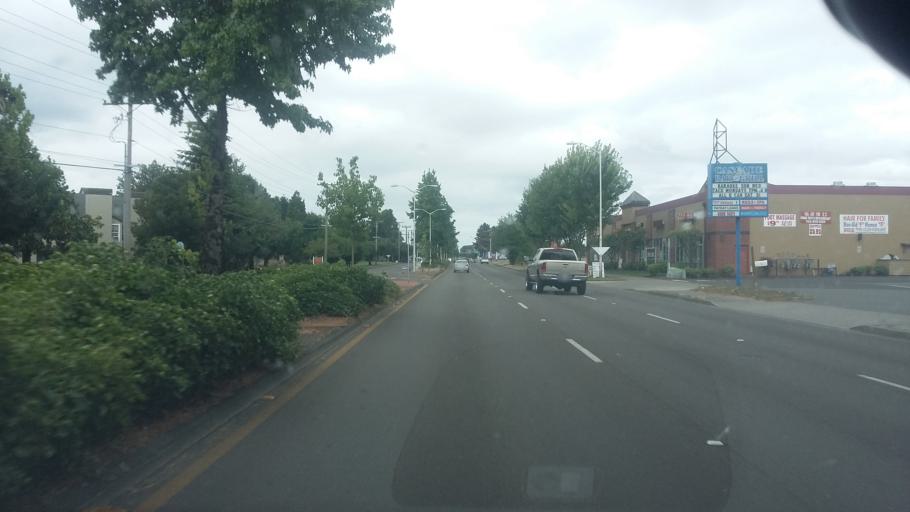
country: US
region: Washington
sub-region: Clark County
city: Mill Plain
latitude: 45.6170
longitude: -122.5172
